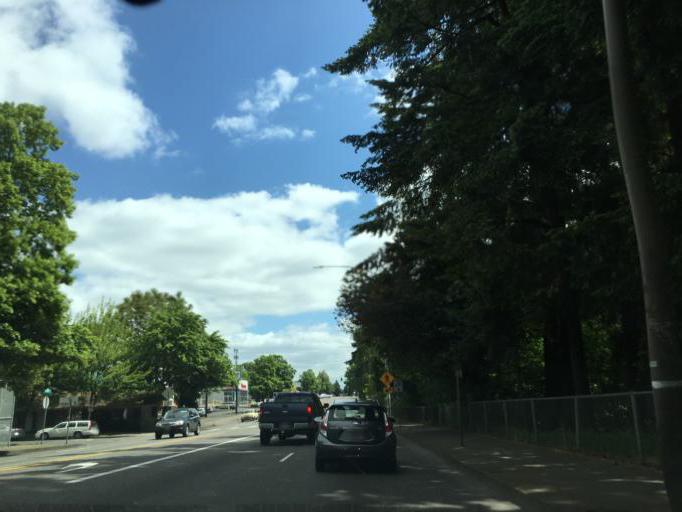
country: US
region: Oregon
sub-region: Multnomah County
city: Lents
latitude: 45.4976
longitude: -122.6171
